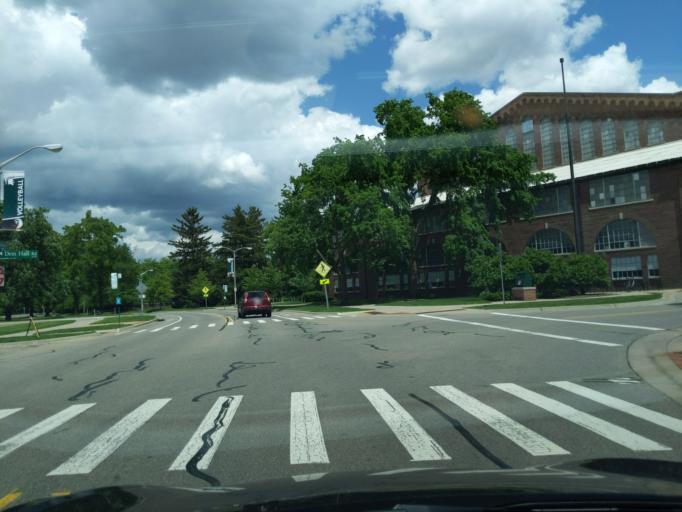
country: US
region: Michigan
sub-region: Ingham County
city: East Lansing
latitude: 42.7298
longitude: -84.4899
